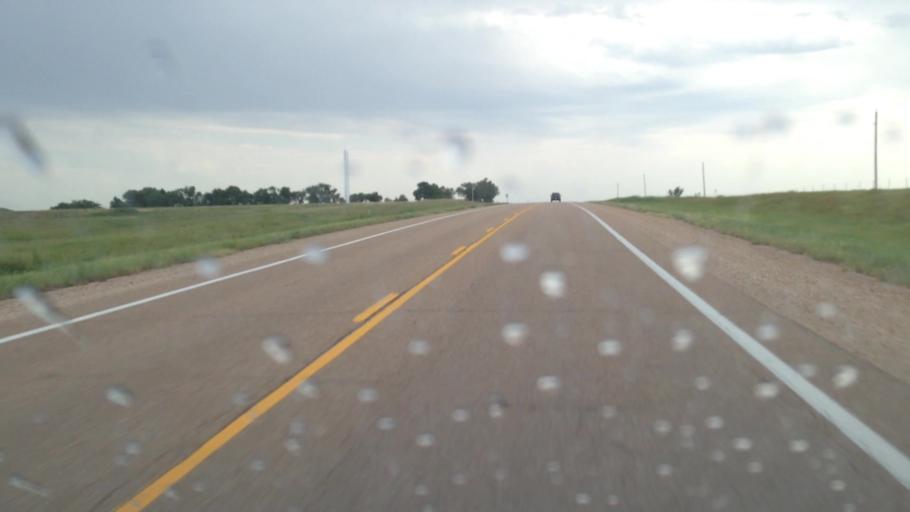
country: US
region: Kansas
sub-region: Coffey County
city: Burlington
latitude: 38.1448
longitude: -95.7392
